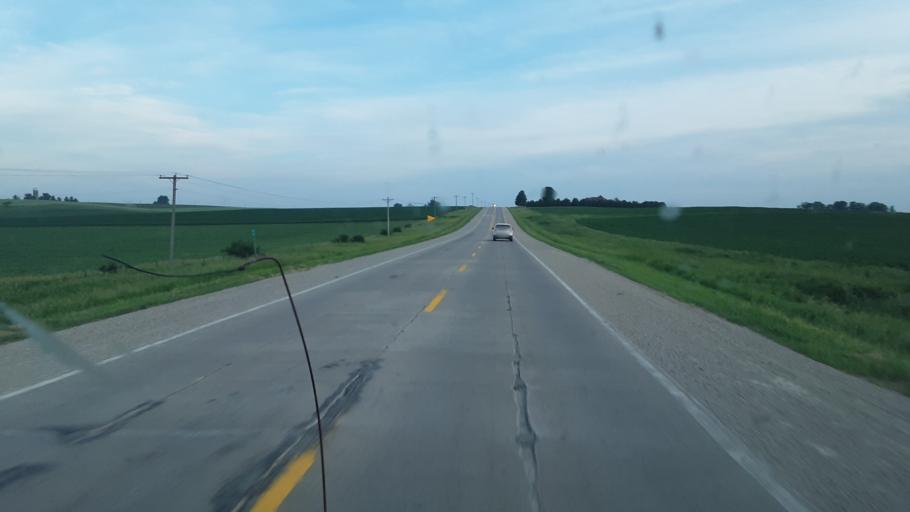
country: US
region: Iowa
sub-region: Benton County
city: Belle Plaine
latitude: 41.8076
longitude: -92.2789
